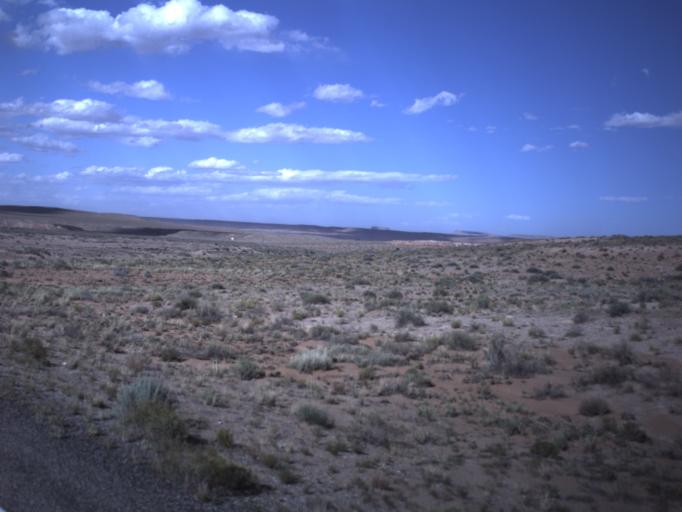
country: US
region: Utah
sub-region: Emery County
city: Ferron
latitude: 38.3193
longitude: -110.6742
